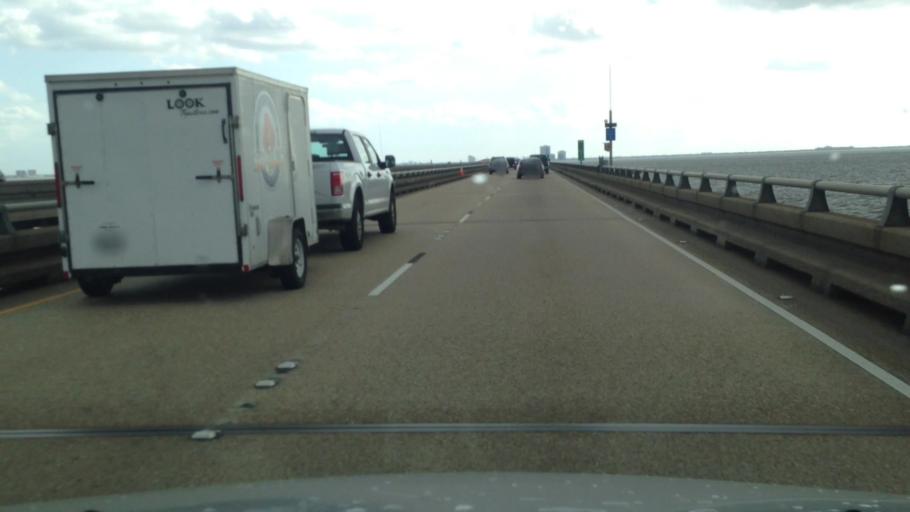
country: US
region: Louisiana
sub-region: Jefferson Parish
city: Metairie
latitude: 30.0877
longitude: -90.1420
